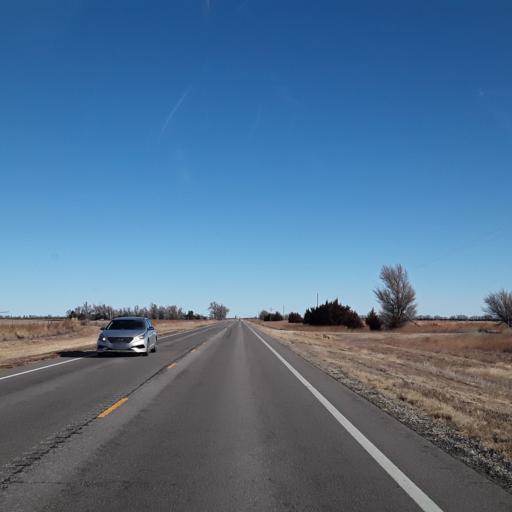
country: US
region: Kansas
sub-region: Pawnee County
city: Larned
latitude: 38.1205
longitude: -99.1785
